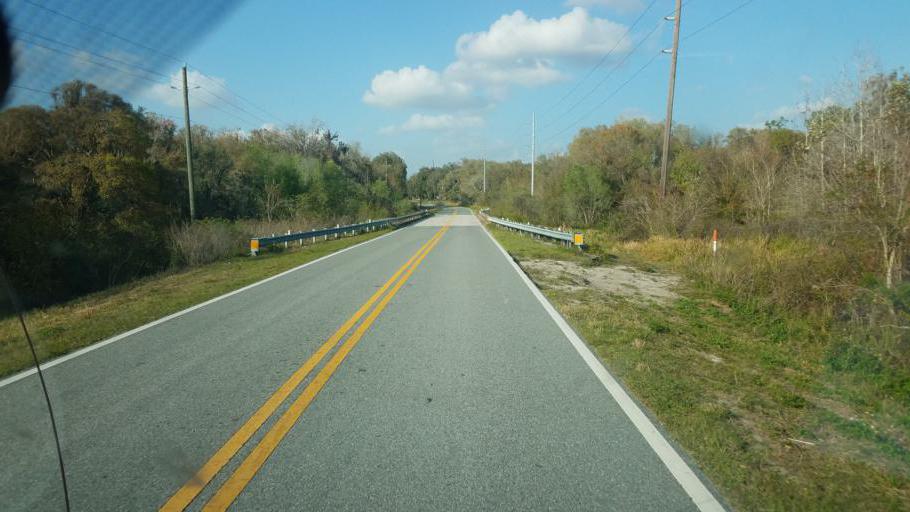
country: US
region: Florida
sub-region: Hardee County
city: Bowling Green
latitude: 27.6060
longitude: -81.9442
